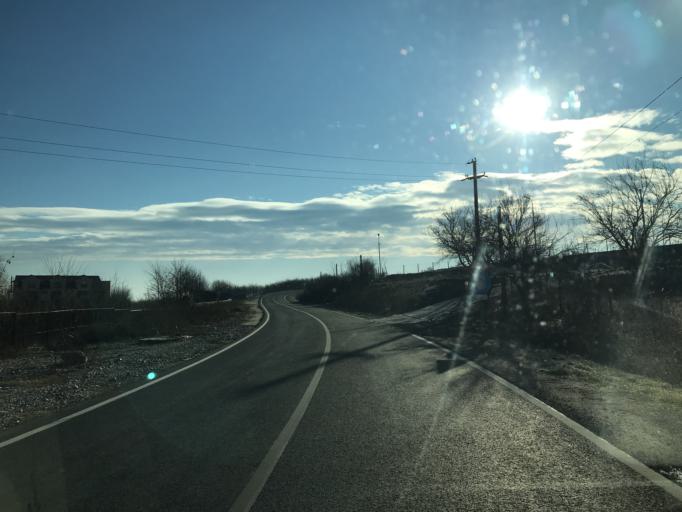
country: RO
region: Olt
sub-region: Comuna Ganeasa
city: Ganeasa
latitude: 44.3968
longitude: 24.2784
